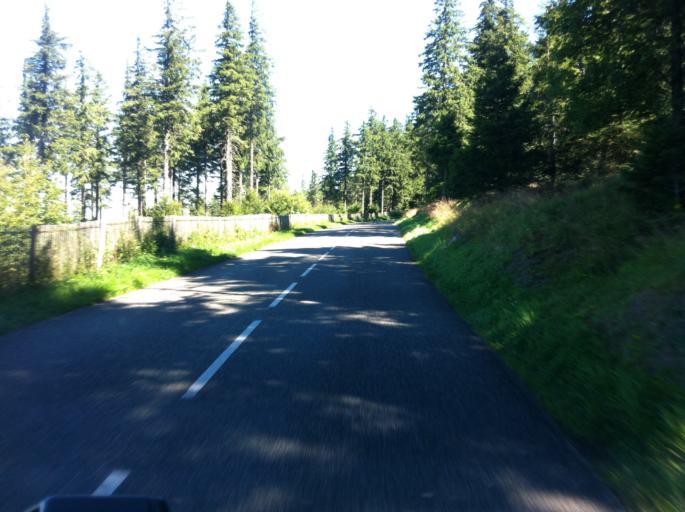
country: FR
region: Alsace
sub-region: Departement du Haut-Rhin
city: Soultzeren
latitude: 48.1341
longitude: 7.0802
